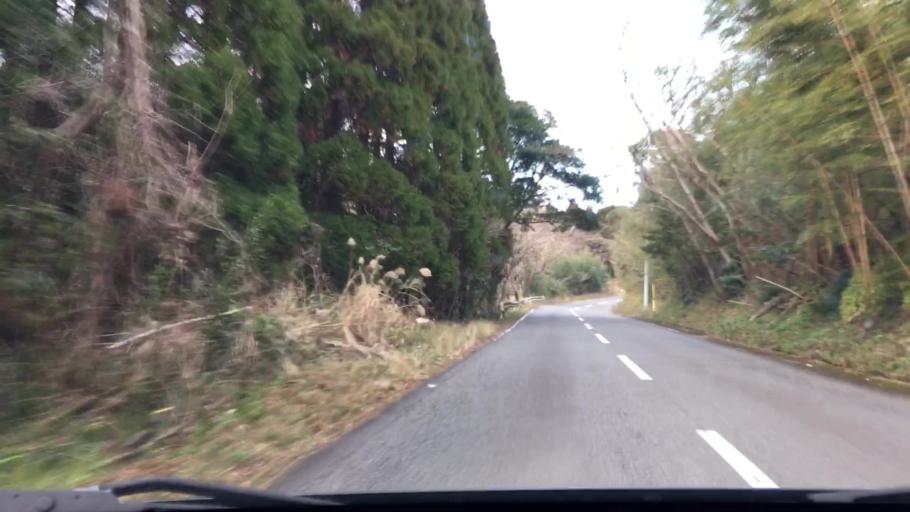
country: JP
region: Miyazaki
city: Nichinan
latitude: 31.6618
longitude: 131.3168
